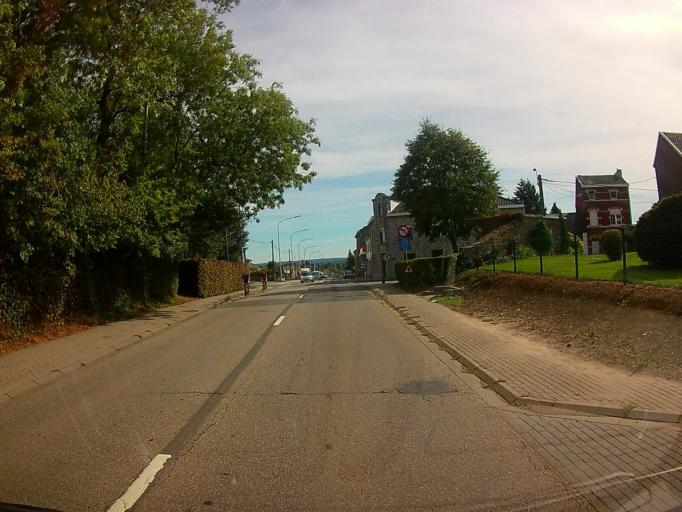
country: BE
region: Wallonia
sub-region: Province de Liege
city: Welkenraedt
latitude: 50.6547
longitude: 5.9925
